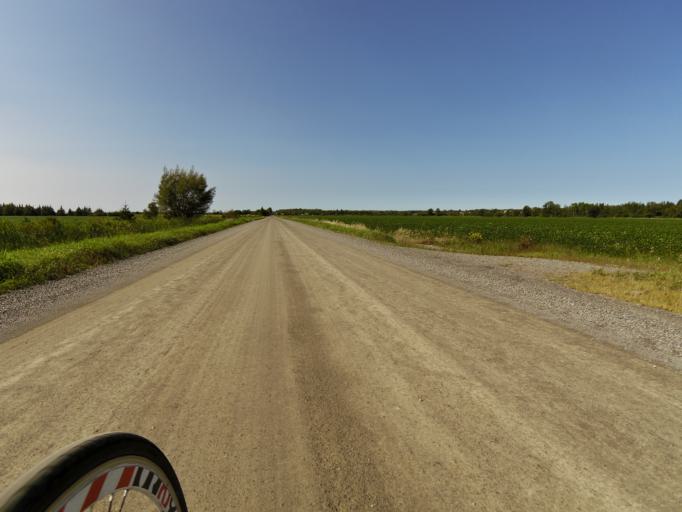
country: CA
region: Ontario
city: Arnprior
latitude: 45.3771
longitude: -76.1466
